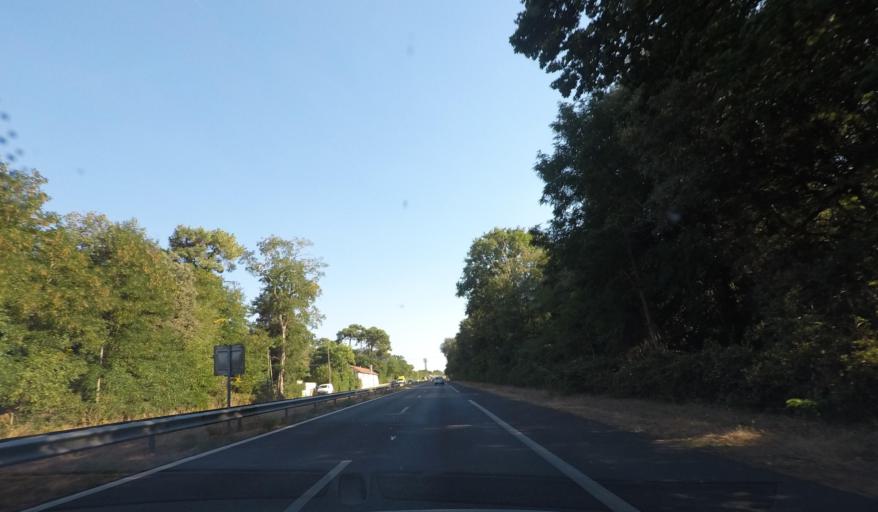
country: FR
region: Pays de la Loire
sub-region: Departement de la Loire-Atlantique
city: Saint-Michel-Chef-Chef
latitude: 47.2021
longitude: -2.1483
